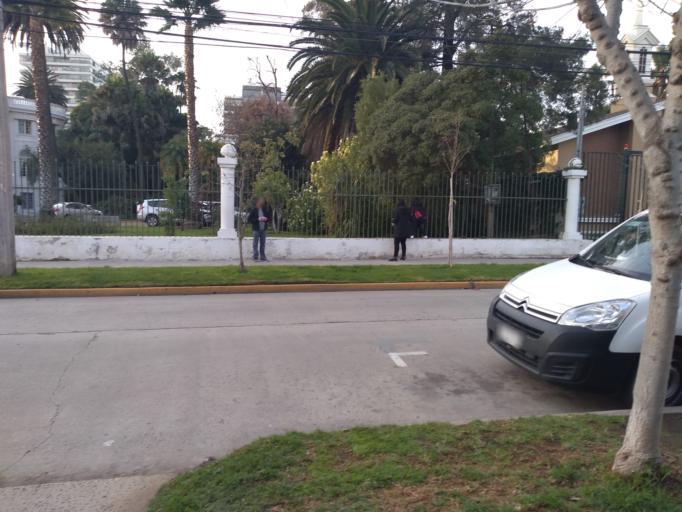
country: CL
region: Valparaiso
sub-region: Provincia de Valparaiso
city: Vina del Mar
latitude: -33.0213
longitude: -71.5462
